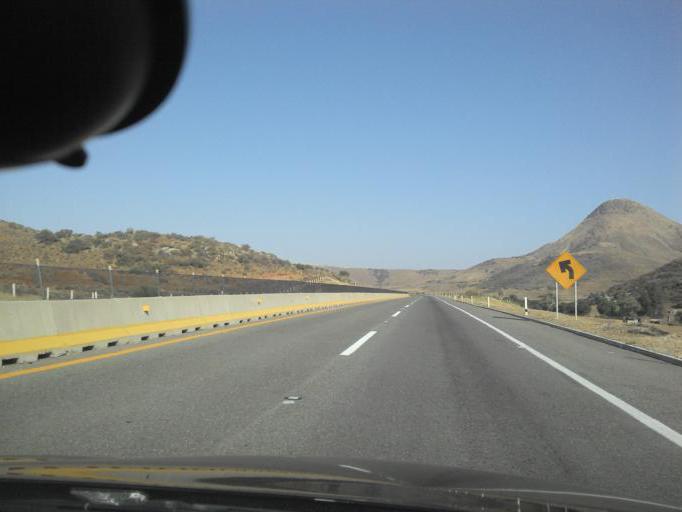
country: MX
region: Baja California
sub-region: Tijuana
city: El Nino
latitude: 32.5477
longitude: -116.7961
